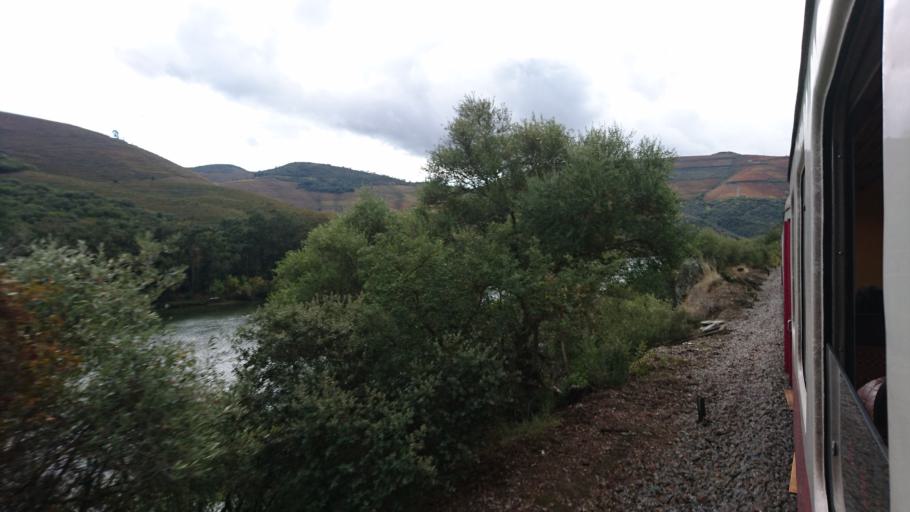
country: PT
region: Viseu
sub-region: Tabuaco
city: Tabuaco
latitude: 41.1915
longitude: -7.5158
